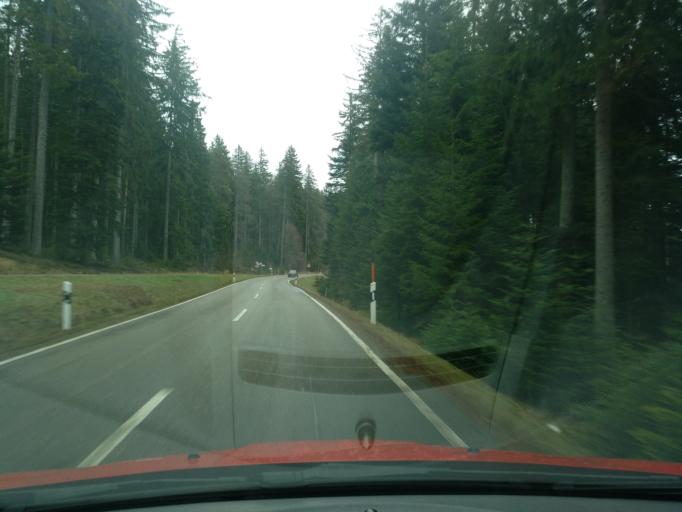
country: DE
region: Baden-Wuerttemberg
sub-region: Freiburg Region
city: Sankt Georgen im Schwarzwald
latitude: 48.1405
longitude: 8.3185
